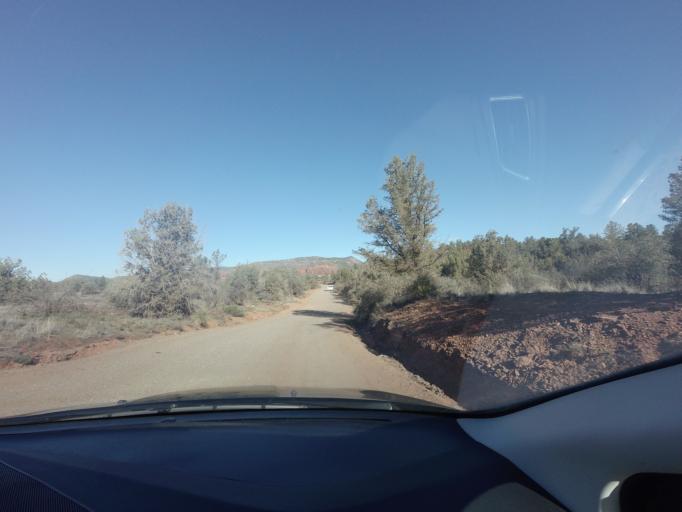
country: US
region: Arizona
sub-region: Yavapai County
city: West Sedona
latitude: 34.8130
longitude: -111.8095
